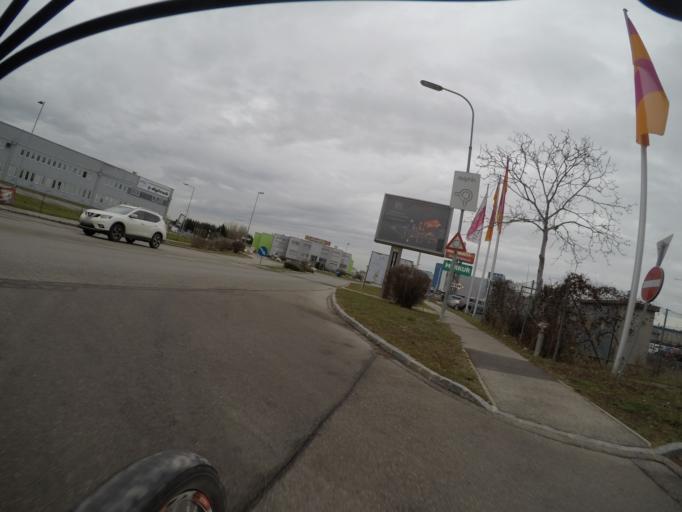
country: AT
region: Lower Austria
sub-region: Politischer Bezirk Modling
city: Brunn am Gebirge
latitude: 48.1084
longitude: 16.3103
